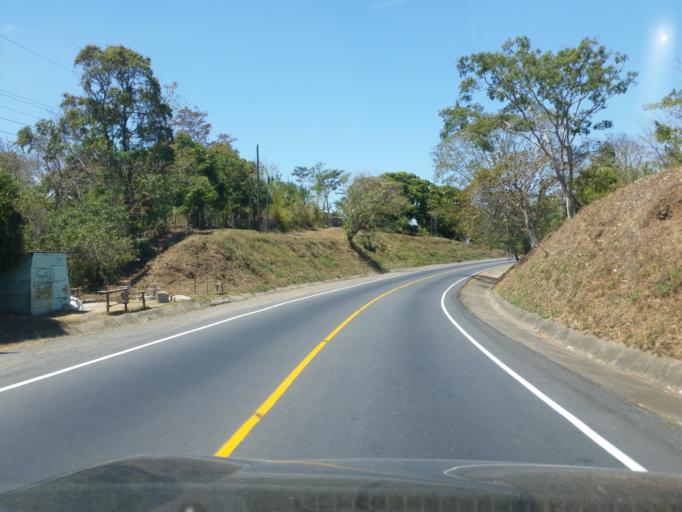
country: NI
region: Masaya
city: Catarina
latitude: 11.9313
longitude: -86.0911
